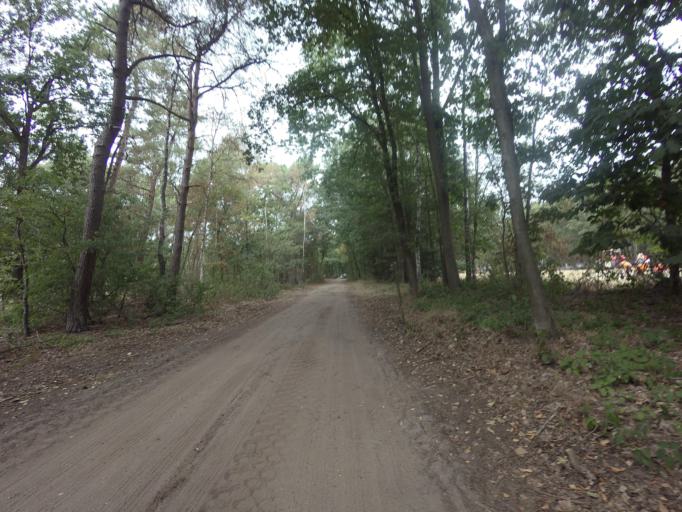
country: NL
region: North Brabant
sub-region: Gemeente Landerd
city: Zeeland
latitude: 51.7040
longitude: 5.6427
